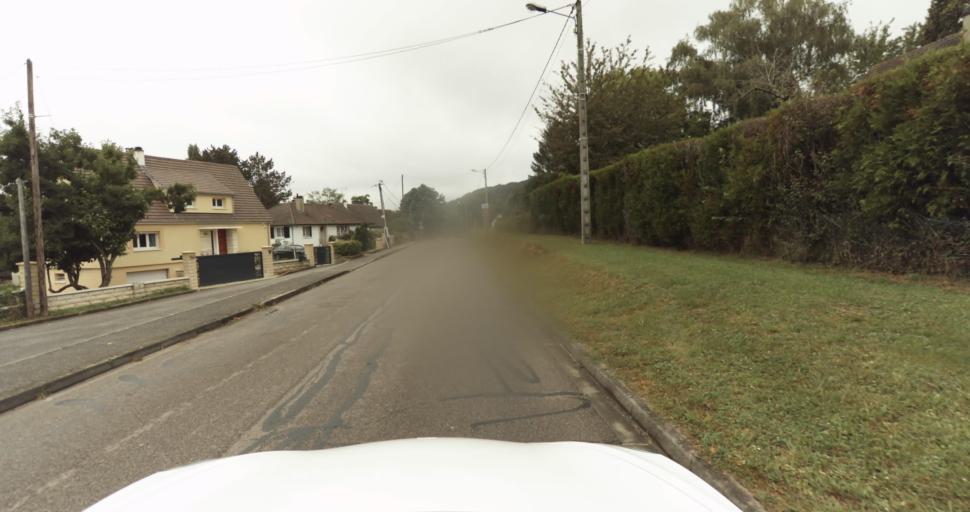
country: FR
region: Haute-Normandie
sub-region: Departement de l'Eure
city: Normanville
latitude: 49.0788
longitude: 1.1624
